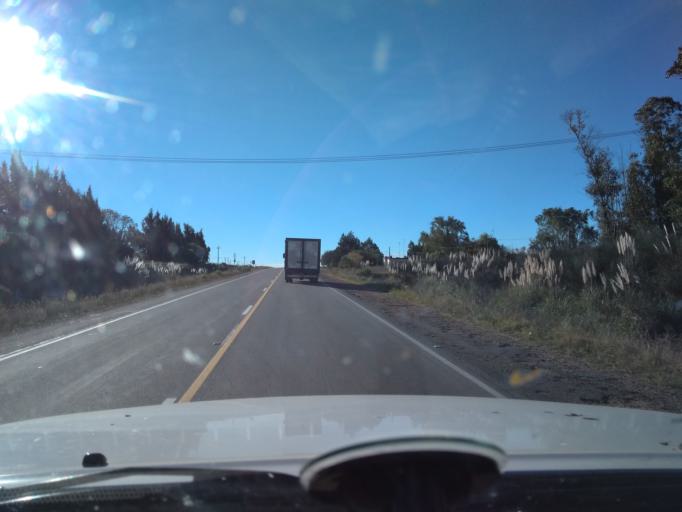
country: UY
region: Canelones
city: Sauce
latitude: -34.5916
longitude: -56.0528
